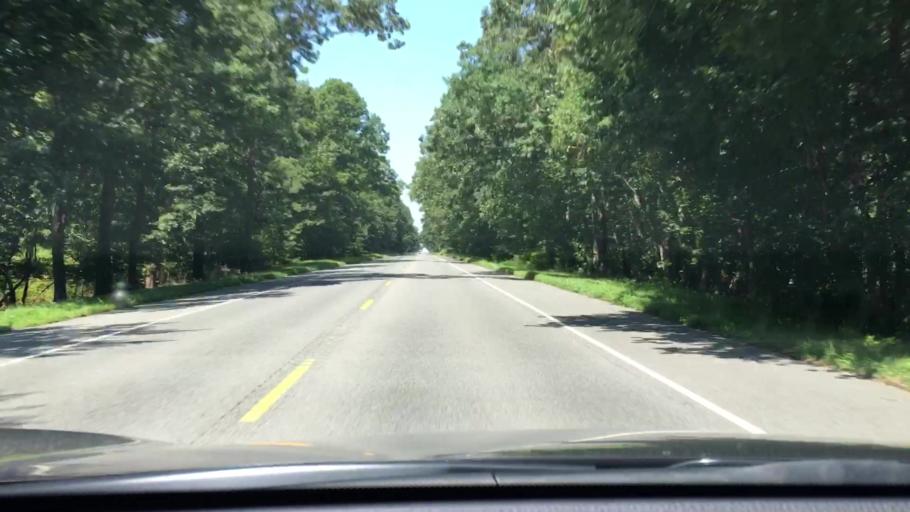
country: US
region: New Jersey
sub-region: Cumberland County
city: Laurel Lake
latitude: 39.3475
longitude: -75.0473
